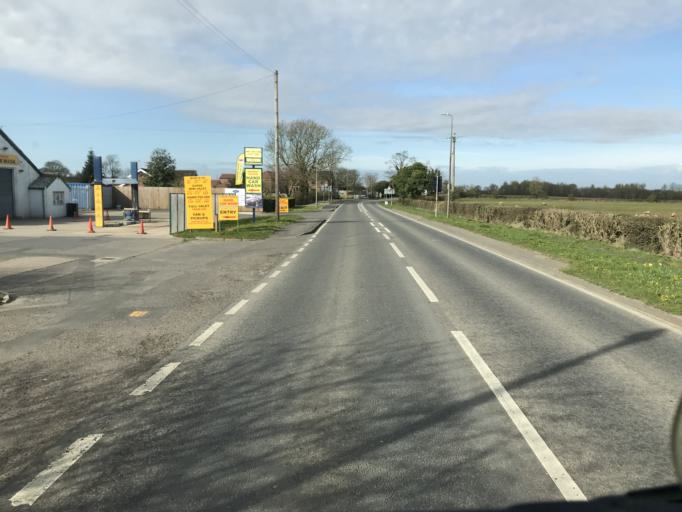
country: GB
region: England
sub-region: Lincolnshire
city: Market Rasen
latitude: 53.3863
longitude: -0.3718
